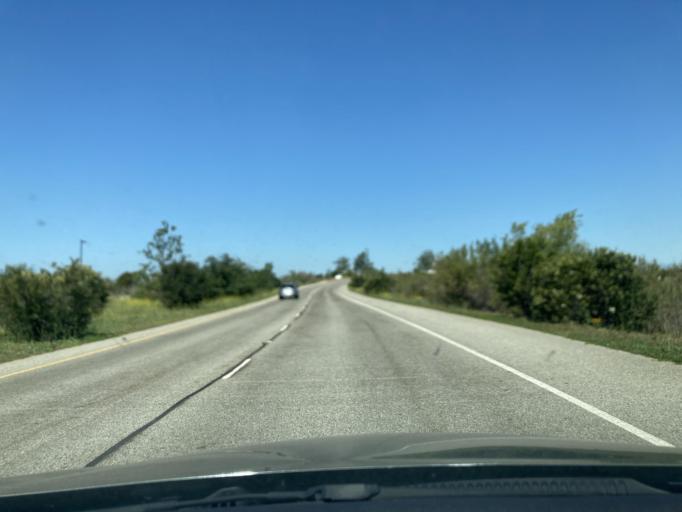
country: US
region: California
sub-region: Ventura County
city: Camarillo
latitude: 34.1696
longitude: -119.0514
